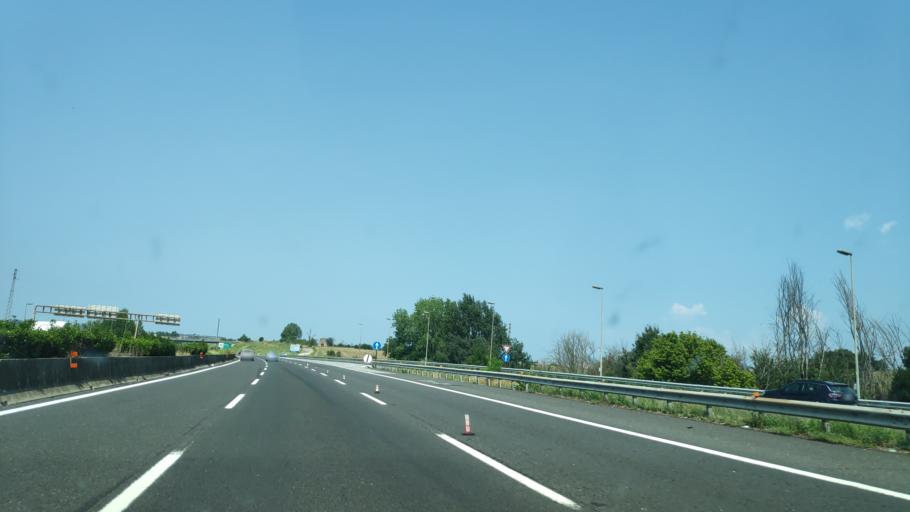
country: IT
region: Latium
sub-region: Citta metropolitana di Roma Capitale
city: Villalba
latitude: 41.9324
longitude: 12.7377
